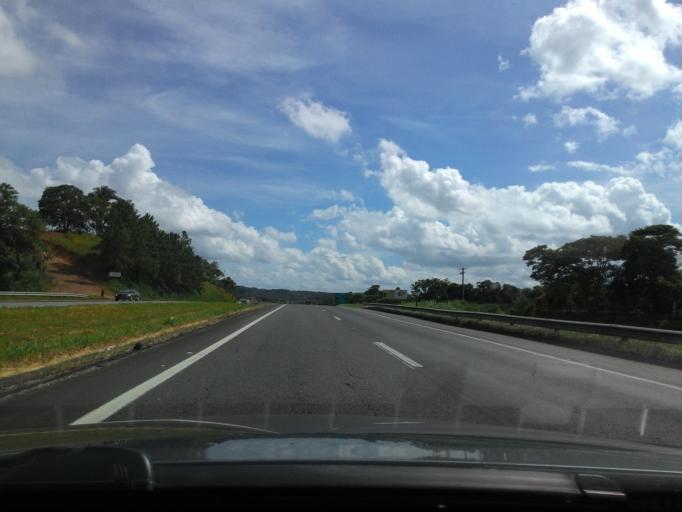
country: BR
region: Sao Paulo
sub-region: Pariquera-Acu
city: Pariquera Acu
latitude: -24.6393
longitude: -47.9135
